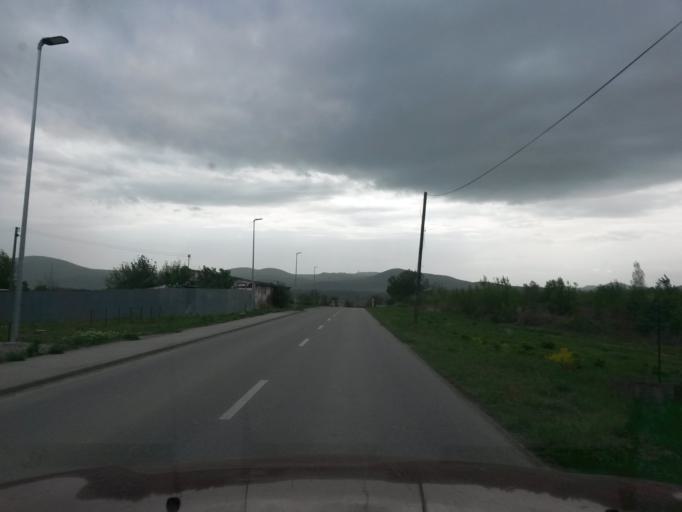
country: HU
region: Borsod-Abauj-Zemplen
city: Gonc
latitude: 48.5459
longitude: 21.2712
